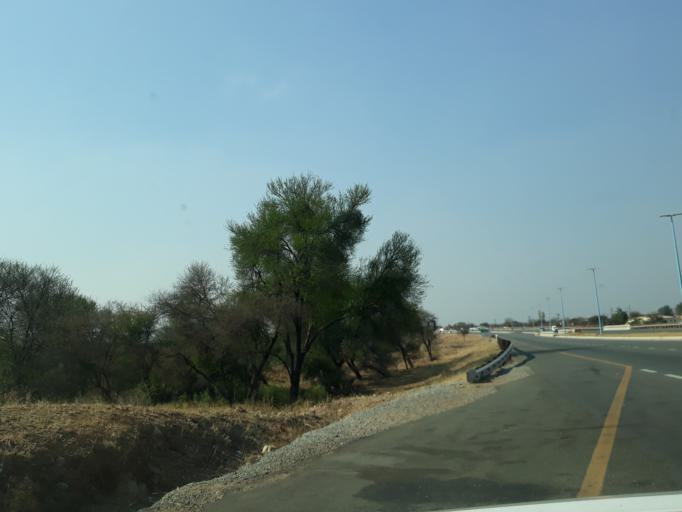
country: BW
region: Central
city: Tonota
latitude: -21.4099
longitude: 27.4509
